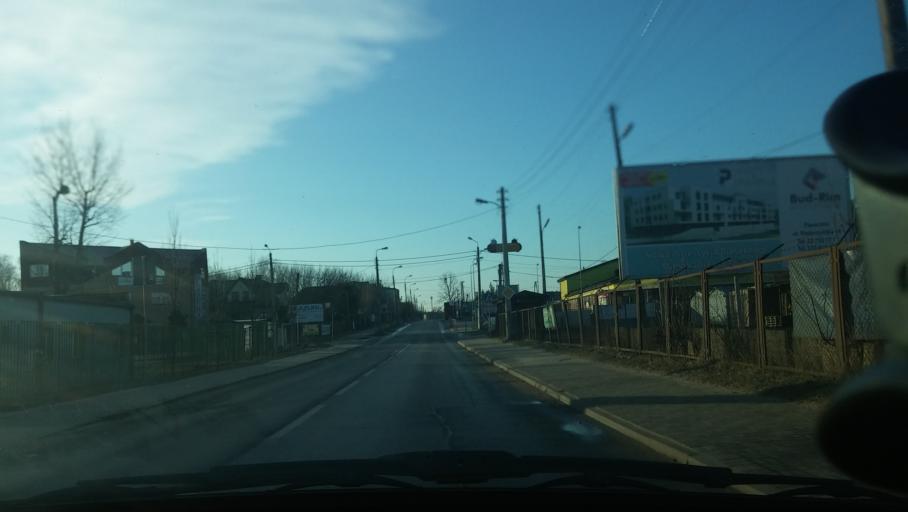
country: PL
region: Masovian Voivodeship
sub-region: Powiat piaseczynski
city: Piaseczno
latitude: 52.0728
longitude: 21.0157
